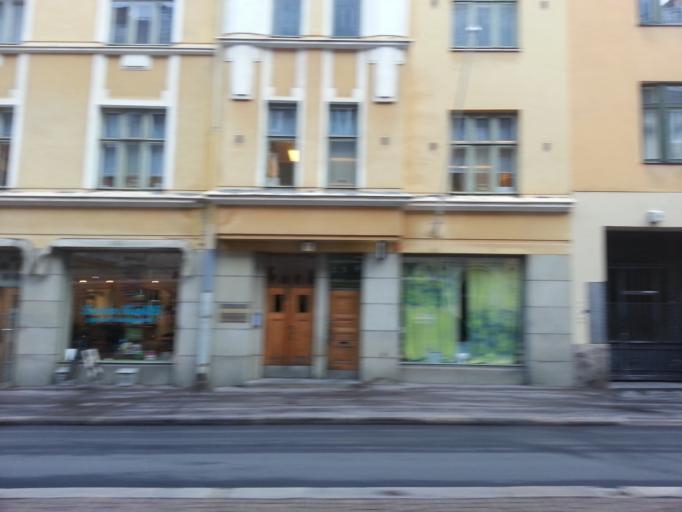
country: FI
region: Uusimaa
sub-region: Helsinki
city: Helsinki
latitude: 60.1712
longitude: 24.9261
